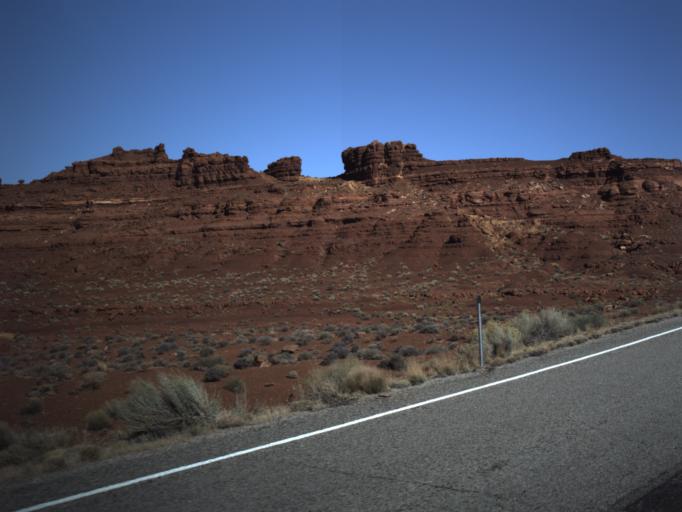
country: US
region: Utah
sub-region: San Juan County
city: Blanding
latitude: 37.8531
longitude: -110.3533
